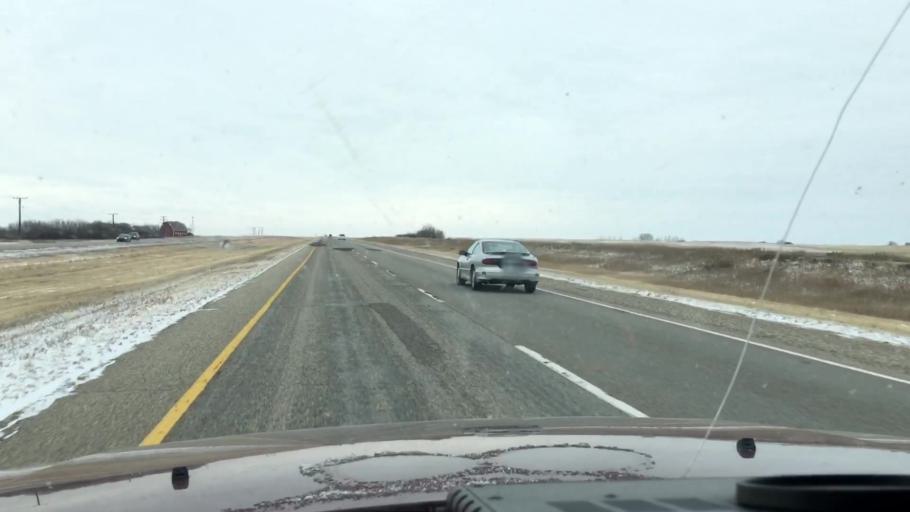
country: CA
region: Saskatchewan
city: Watrous
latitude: 51.4230
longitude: -106.1950
